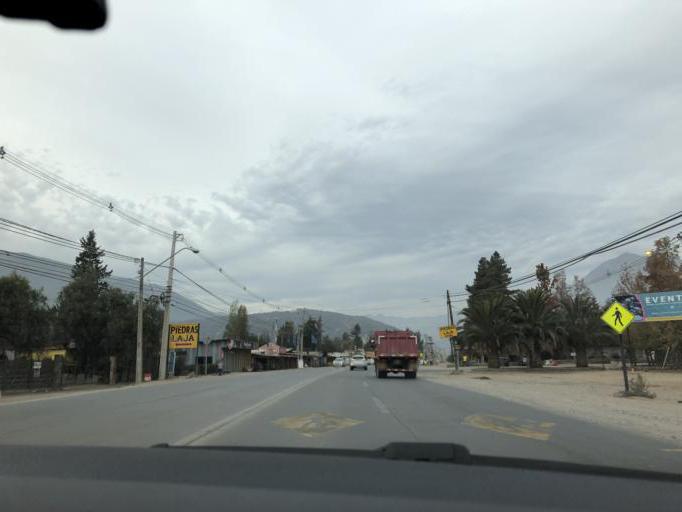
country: CL
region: Santiago Metropolitan
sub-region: Provincia de Cordillera
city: Puente Alto
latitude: -33.5985
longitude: -70.5261
